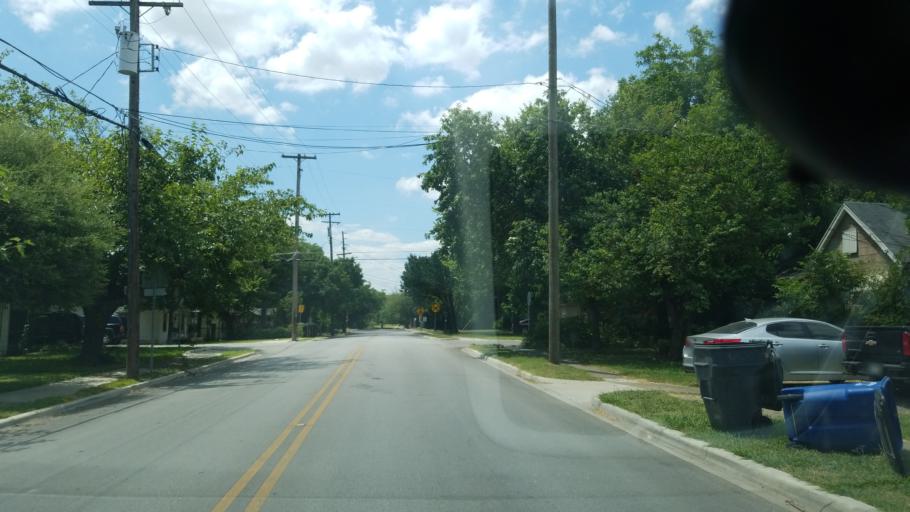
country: US
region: Texas
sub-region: Dallas County
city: Cockrell Hill
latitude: 32.7329
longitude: -96.8443
